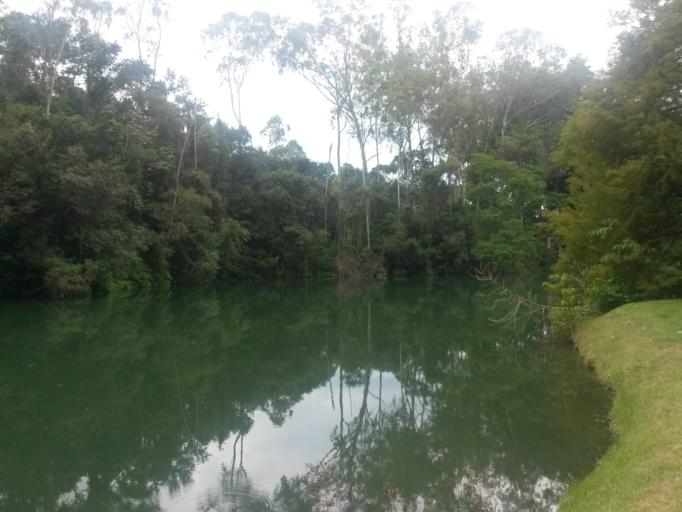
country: BR
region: Minas Gerais
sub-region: Brumadinho
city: Brumadinho
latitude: -20.1206
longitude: -44.2199
